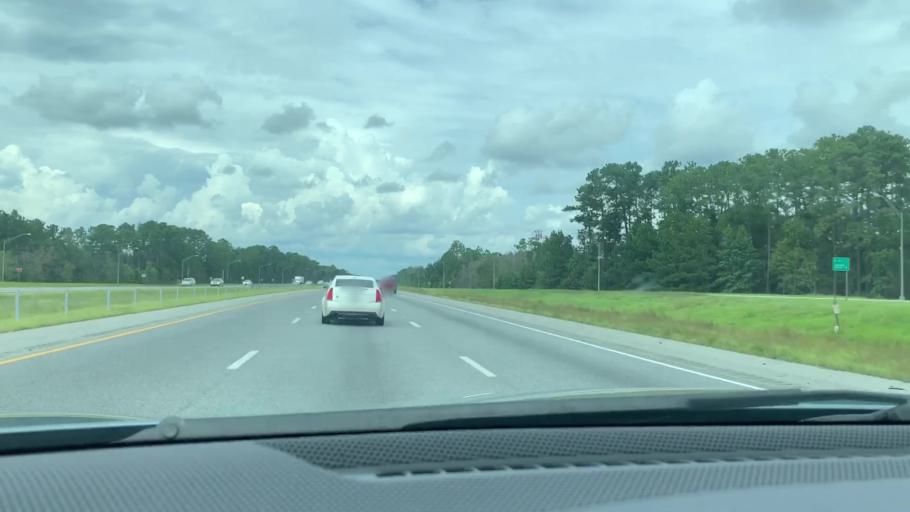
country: US
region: Georgia
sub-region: McIntosh County
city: Darien
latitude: 31.4788
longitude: -81.4470
